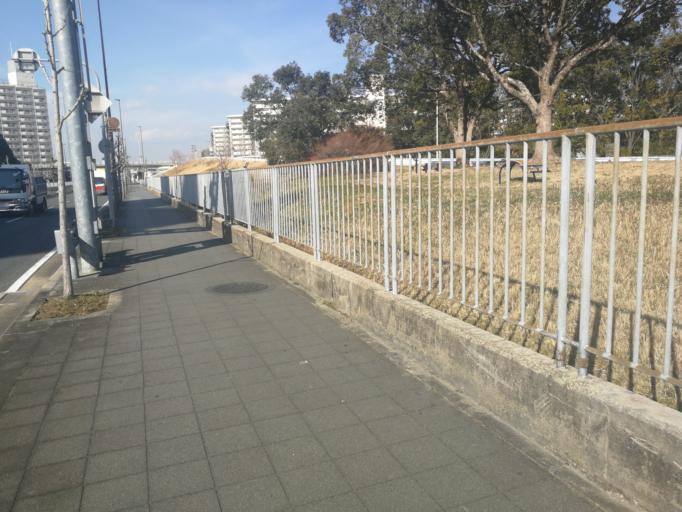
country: JP
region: Kyoto
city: Uji
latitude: 34.9186
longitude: 135.7789
